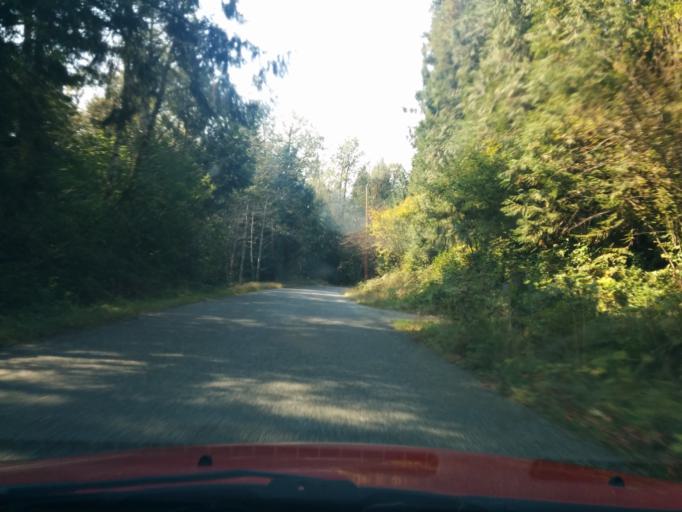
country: US
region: Washington
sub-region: Snohomish County
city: Darrington
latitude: 48.5302
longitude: -121.3969
